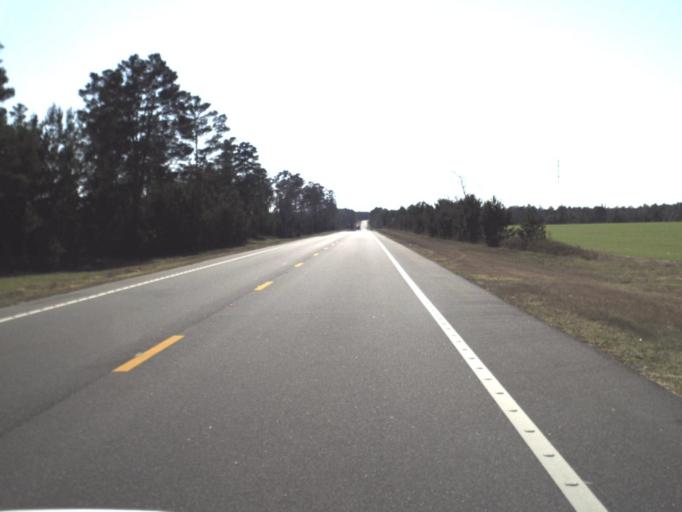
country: US
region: Florida
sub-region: Bay County
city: Youngstown
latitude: 30.4312
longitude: -85.2854
